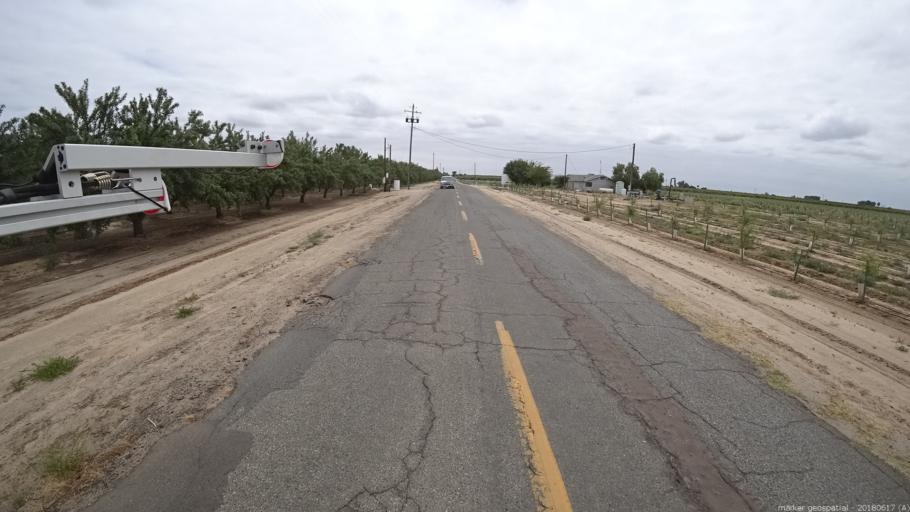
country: US
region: California
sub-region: Madera County
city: Fairmead
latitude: 36.9963
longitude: -120.2149
